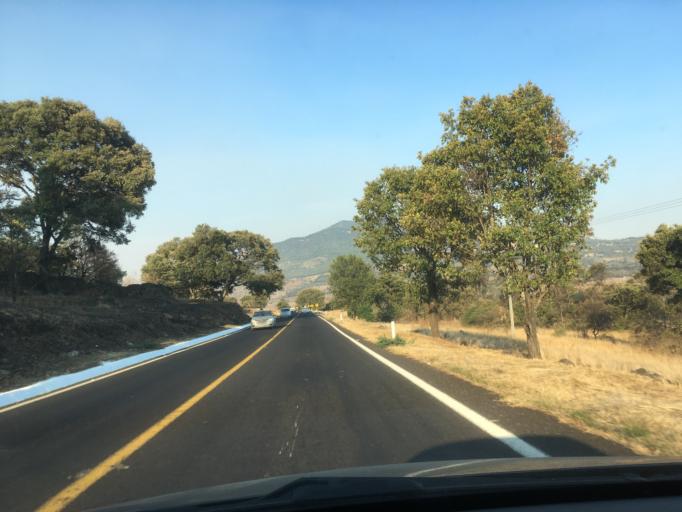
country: MX
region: Michoacan
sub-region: Morelia
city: Iratzio
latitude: 19.6279
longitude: -101.4336
